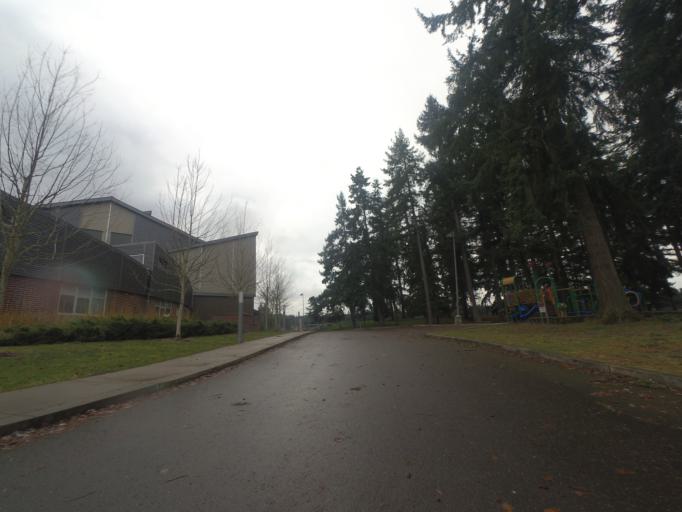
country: US
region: Washington
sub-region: Pierce County
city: University Place
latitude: 47.2236
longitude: -122.5545
